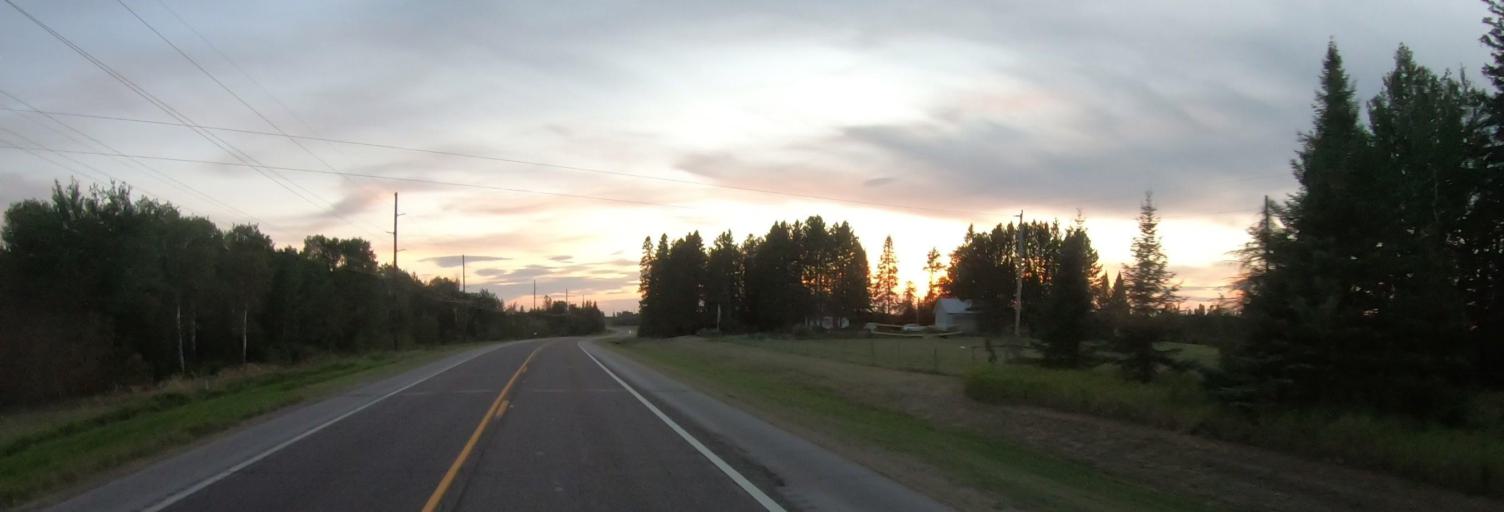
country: US
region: Minnesota
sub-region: Saint Louis County
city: Parkville
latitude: 47.8464
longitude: -92.5528
